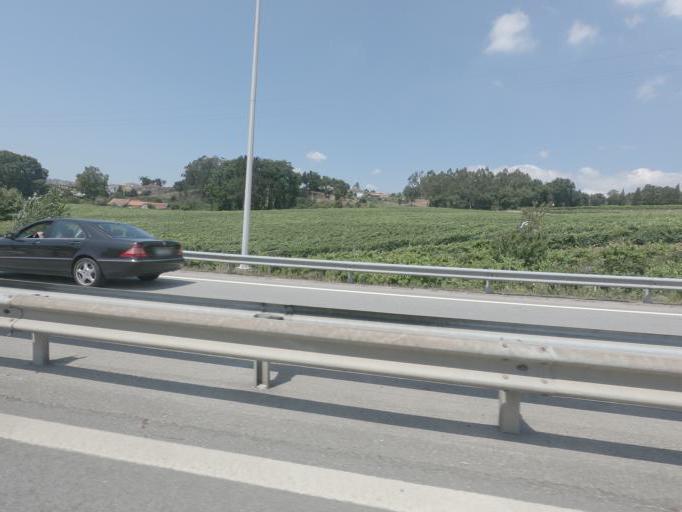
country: PT
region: Porto
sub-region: Paredes
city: Paredes
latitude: 41.2024
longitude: -8.3125
